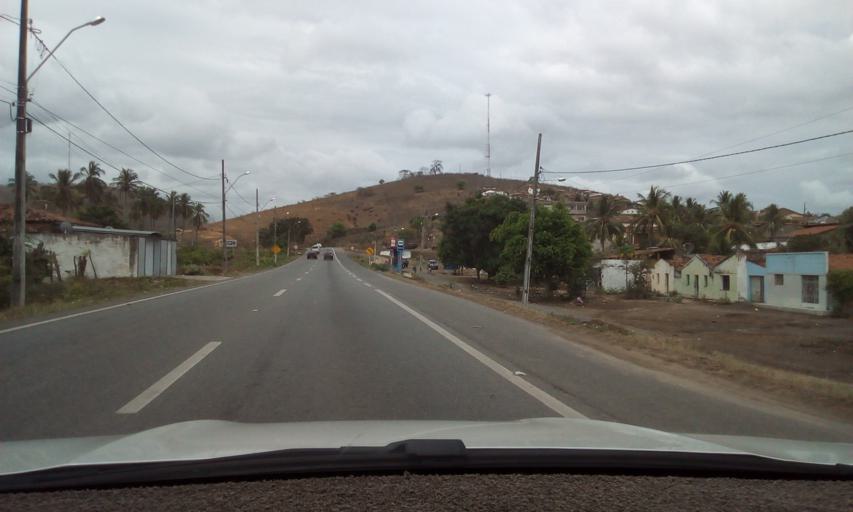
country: BR
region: Paraiba
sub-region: Inga
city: Inga
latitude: -7.2476
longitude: -35.6676
